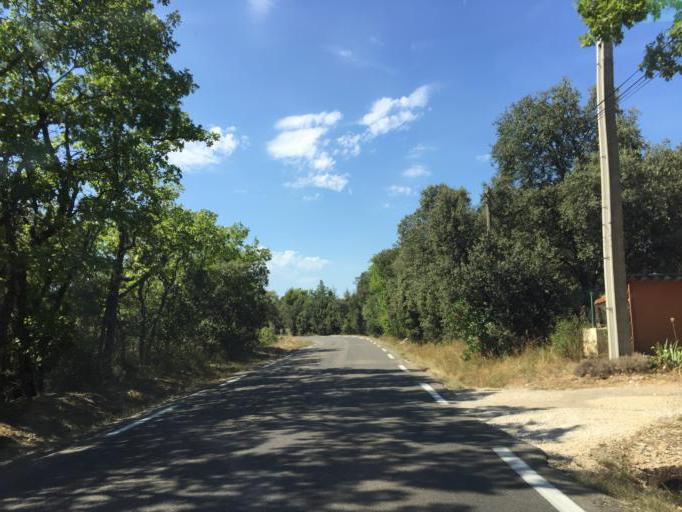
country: FR
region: Provence-Alpes-Cote d'Azur
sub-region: Departement du Vaucluse
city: Saint-Didier
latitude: 44.0145
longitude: 5.1344
